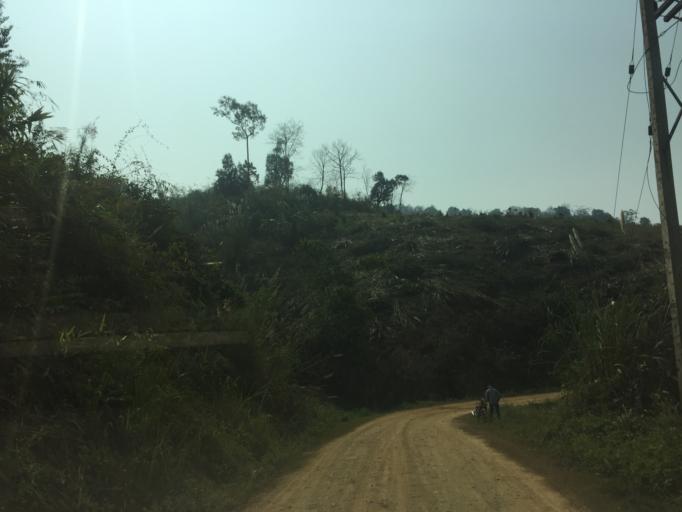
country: TH
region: Phayao
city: Phu Sang
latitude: 19.6233
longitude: 100.5394
